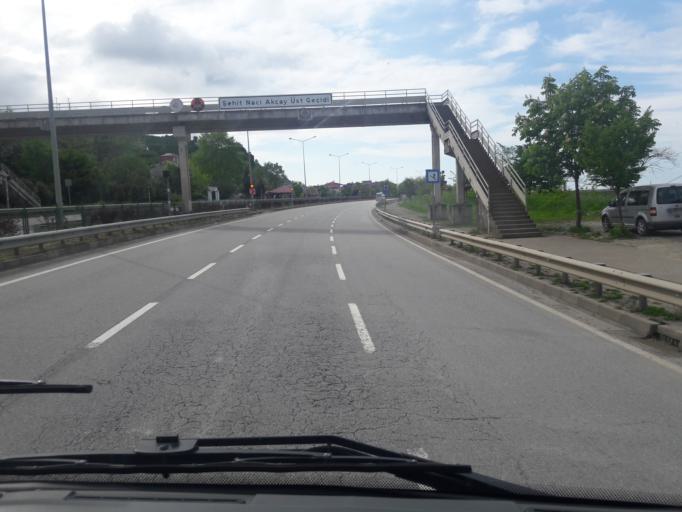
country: TR
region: Giresun
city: Piraziz
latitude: 40.9540
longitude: 38.1228
